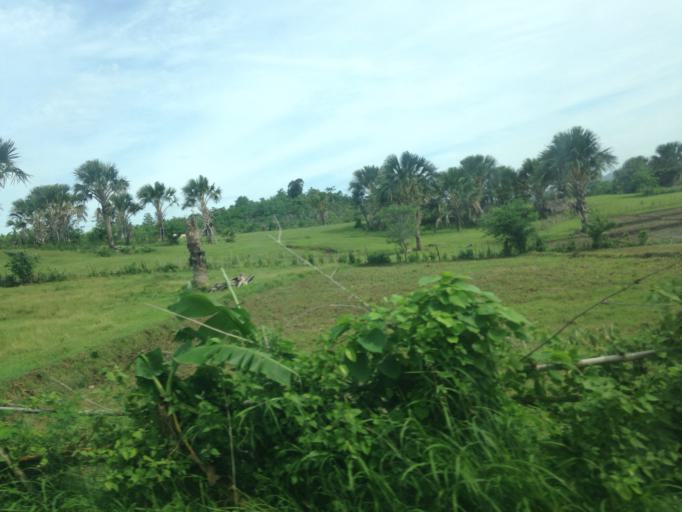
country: PH
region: Mimaropa
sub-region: Province of Mindoro Oriental
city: Bulalacao
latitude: 12.3835
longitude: 121.3541
